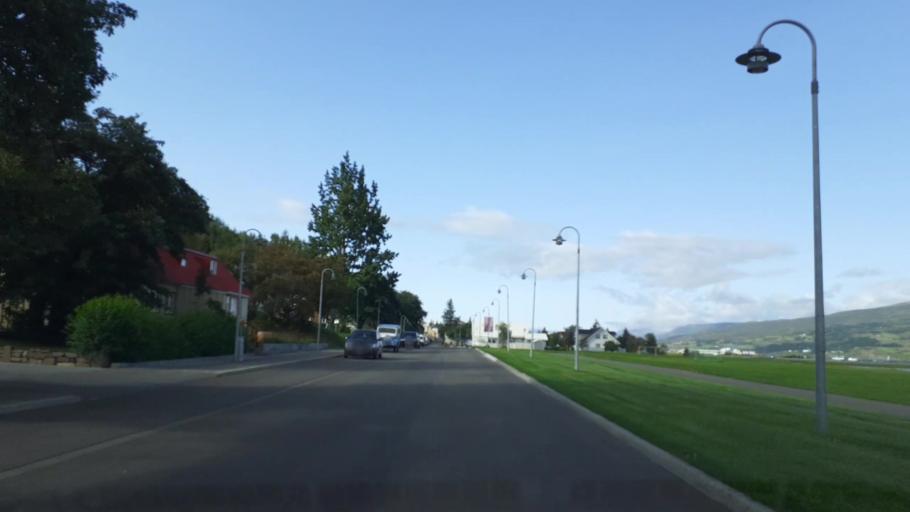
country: IS
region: Northeast
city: Akureyri
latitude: 65.6673
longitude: -18.0851
